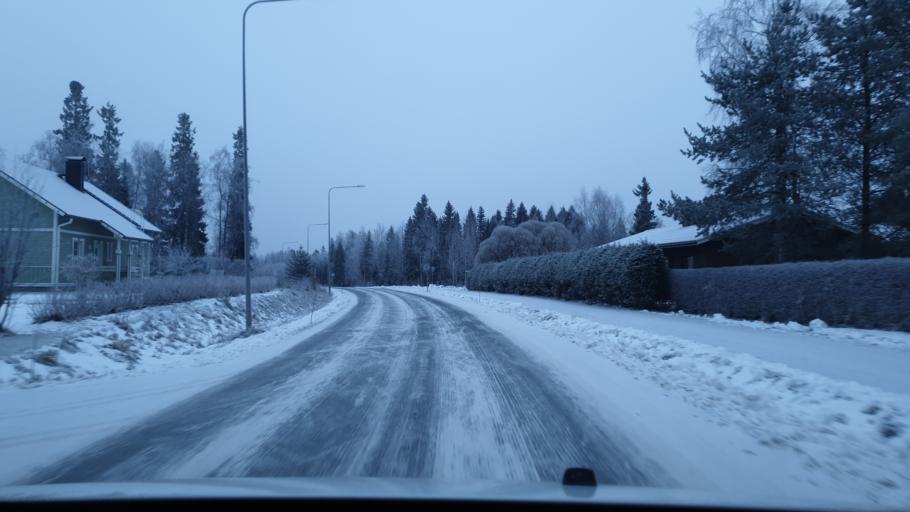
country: FI
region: Lapland
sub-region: Kemi-Tornio
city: Kemi
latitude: 65.7385
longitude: 24.6075
